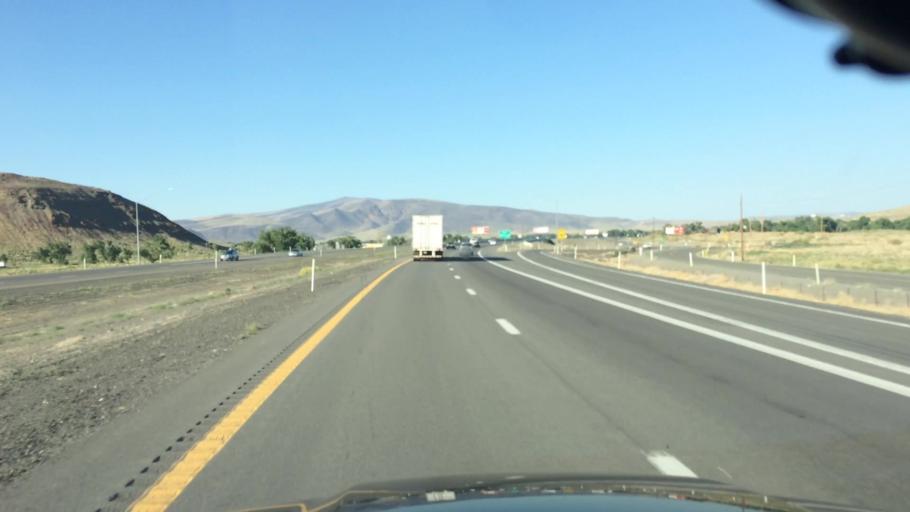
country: US
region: Nevada
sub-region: Lyon County
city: Fernley
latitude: 39.6143
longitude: -119.3130
